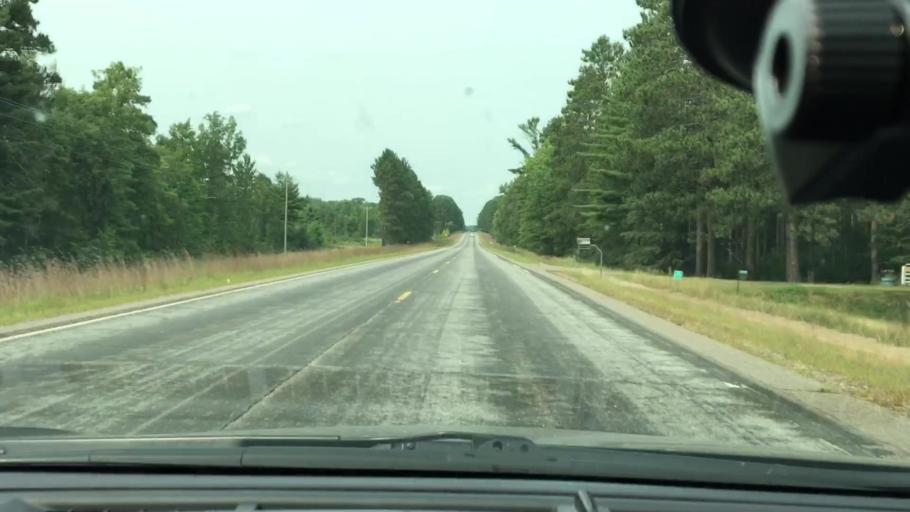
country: US
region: Minnesota
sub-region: Crow Wing County
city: Cross Lake
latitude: 46.7694
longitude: -93.9664
